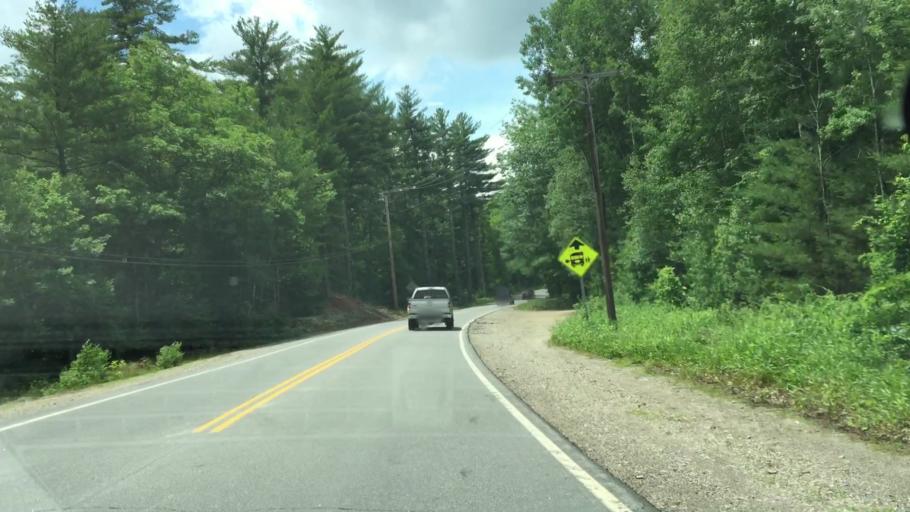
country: US
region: New Hampshire
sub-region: Grafton County
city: Holderness
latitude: 43.7426
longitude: -71.5786
